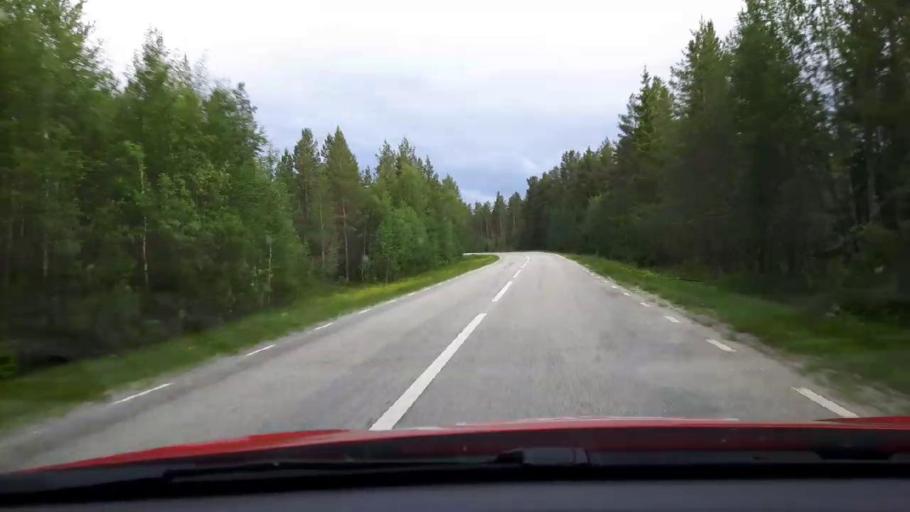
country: SE
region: Jaemtland
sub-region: Bergs Kommun
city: Hoverberg
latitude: 62.6566
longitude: 14.0550
